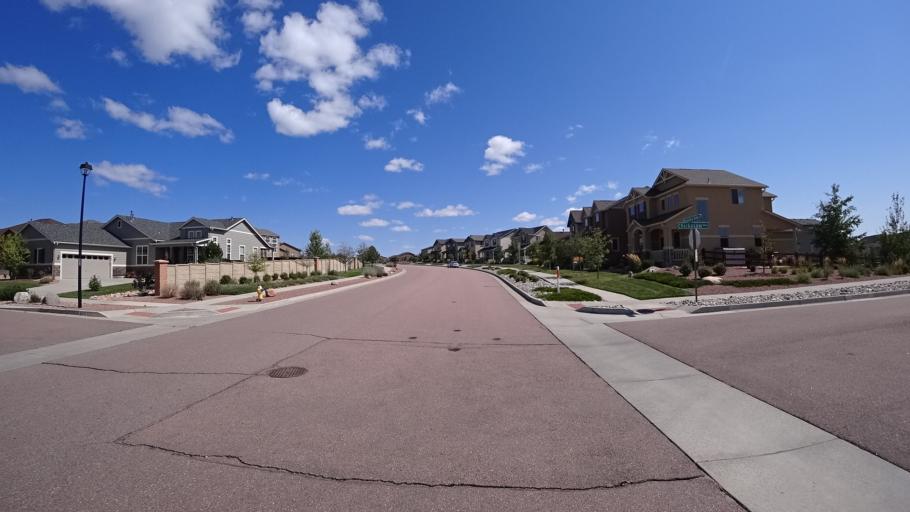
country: US
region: Colorado
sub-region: El Paso County
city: Cimarron Hills
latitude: 38.9279
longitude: -104.6901
